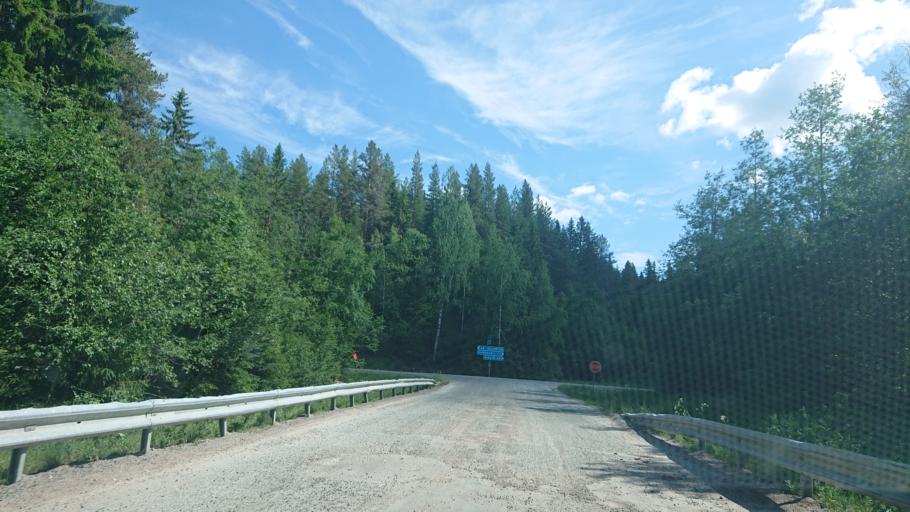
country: SE
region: Vaesternorrland
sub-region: Solleftea Kommun
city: Solleftea
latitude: 62.9665
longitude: 17.1831
